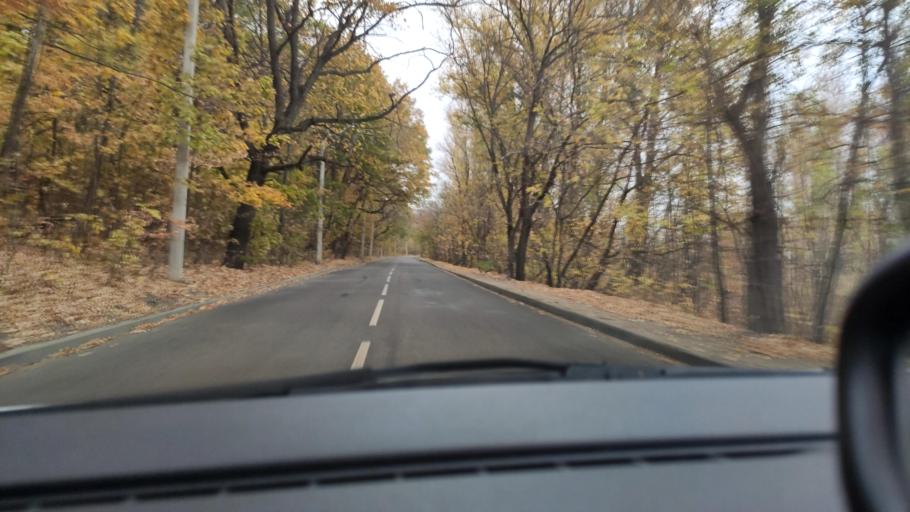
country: RU
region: Voronezj
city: Voronezh
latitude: 51.7231
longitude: 39.2367
